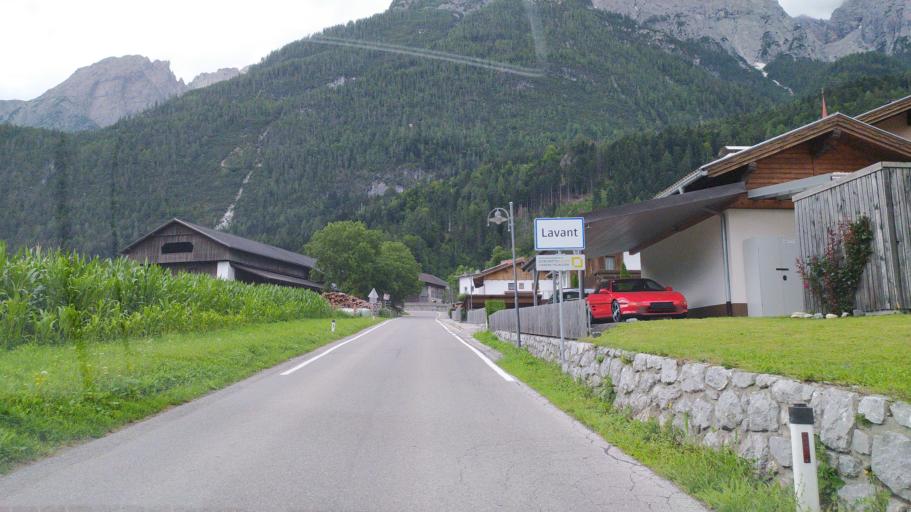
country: AT
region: Tyrol
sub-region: Politischer Bezirk Lienz
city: Lavant
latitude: 46.7989
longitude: 12.8394
